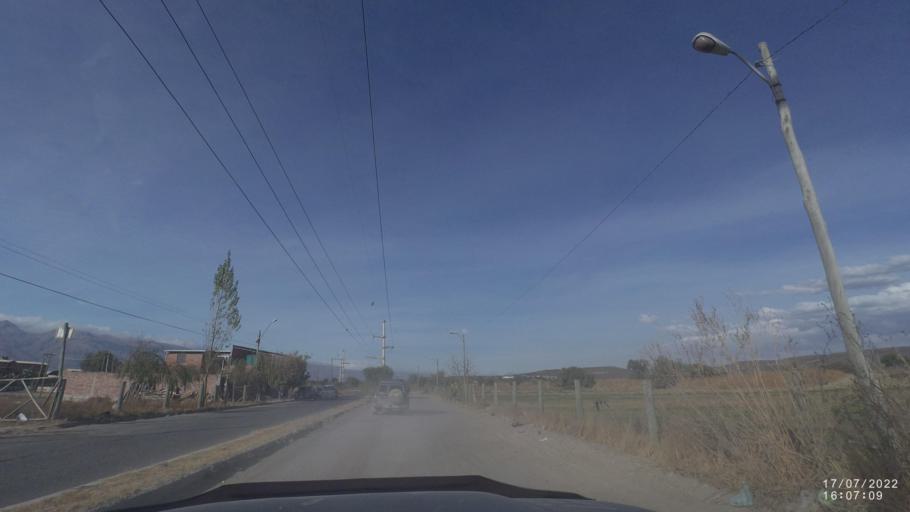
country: BO
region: Cochabamba
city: Sipe Sipe
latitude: -17.4149
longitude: -66.2746
